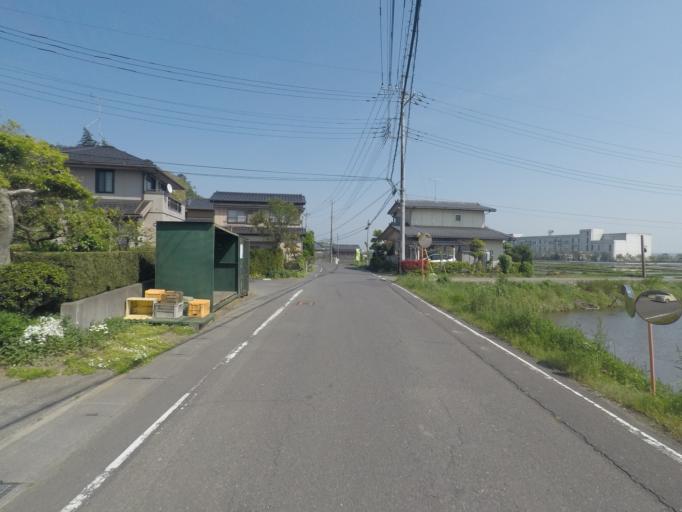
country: JP
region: Ibaraki
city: Inashiki
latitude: 36.0673
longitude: 140.3213
